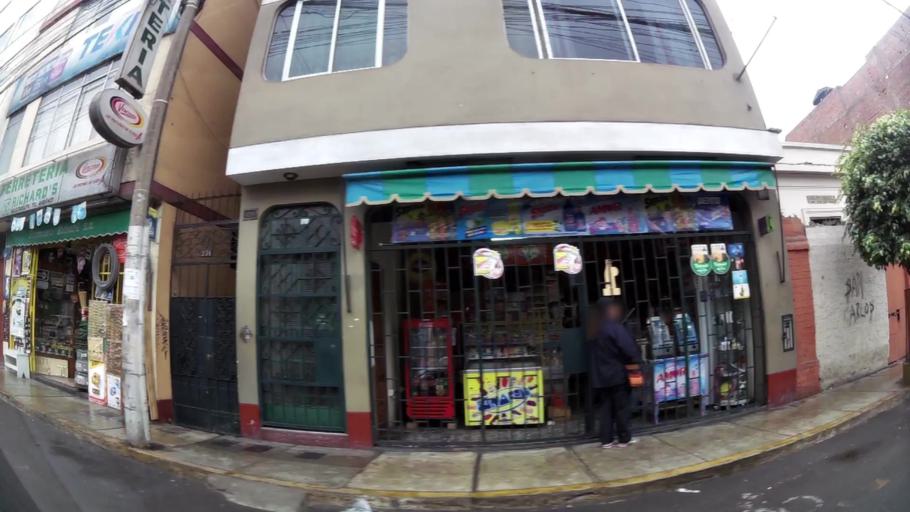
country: PE
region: Lima
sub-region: Lima
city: San Isidro
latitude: -12.1179
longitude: -77.0248
